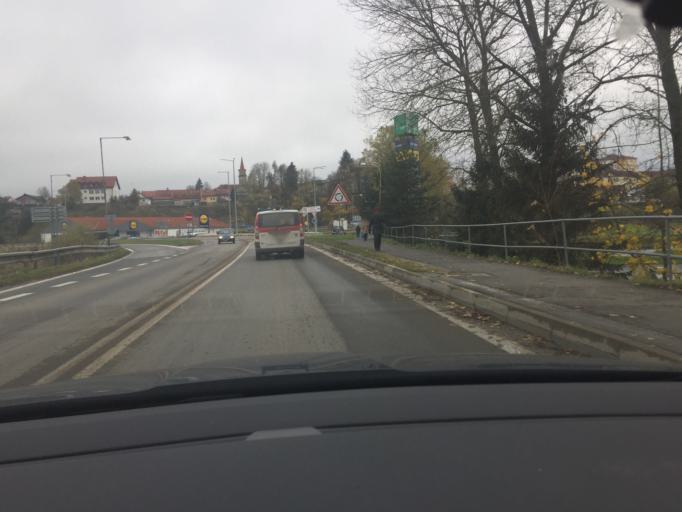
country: SK
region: Presovsky
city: Stara L'ubovna
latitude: 49.3060
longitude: 20.6868
